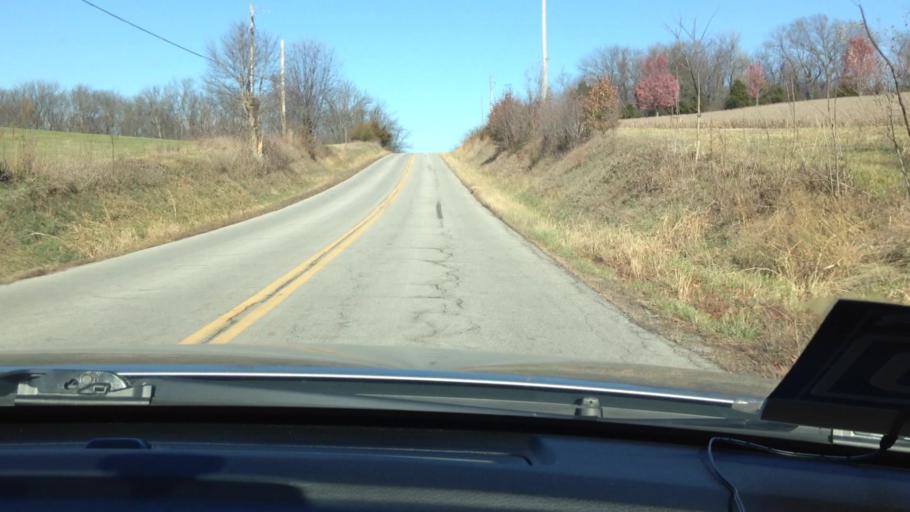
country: US
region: Missouri
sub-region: Platte County
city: Weston
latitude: 39.4590
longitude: -94.9007
